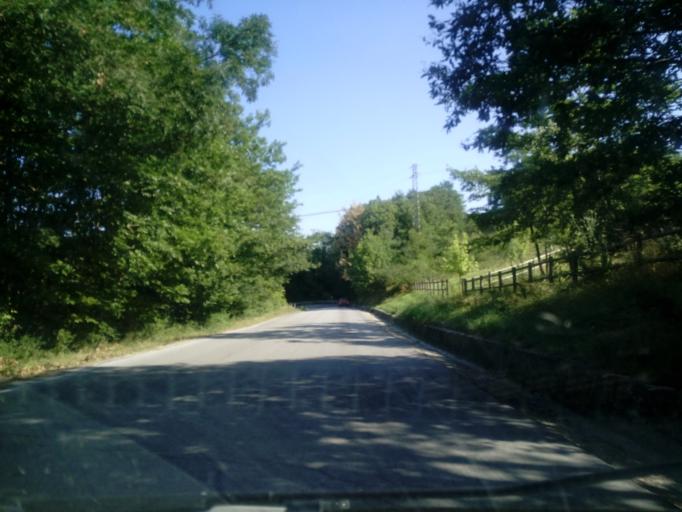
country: IT
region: Molise
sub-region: Provincia di Campobasso
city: Jelsi
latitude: 41.5133
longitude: 14.7924
